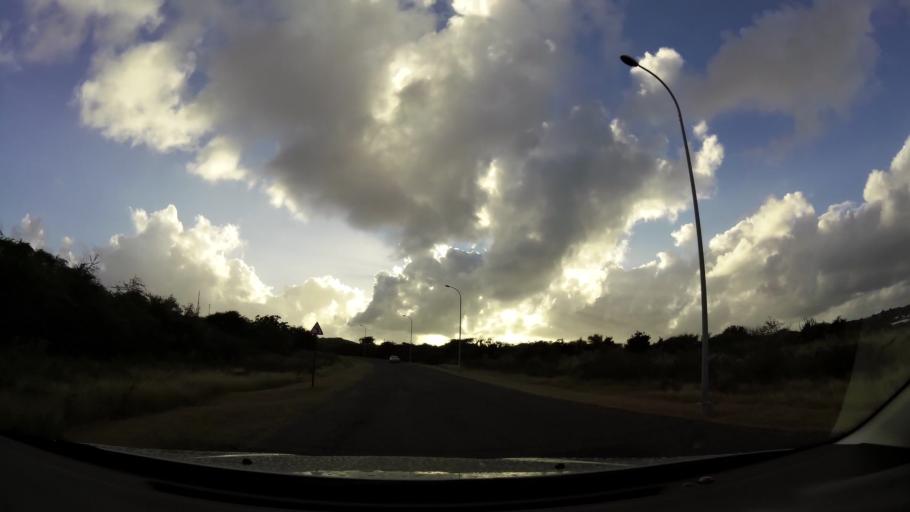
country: AG
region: Saint John
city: Saint John's
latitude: 17.1571
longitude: -61.8276
